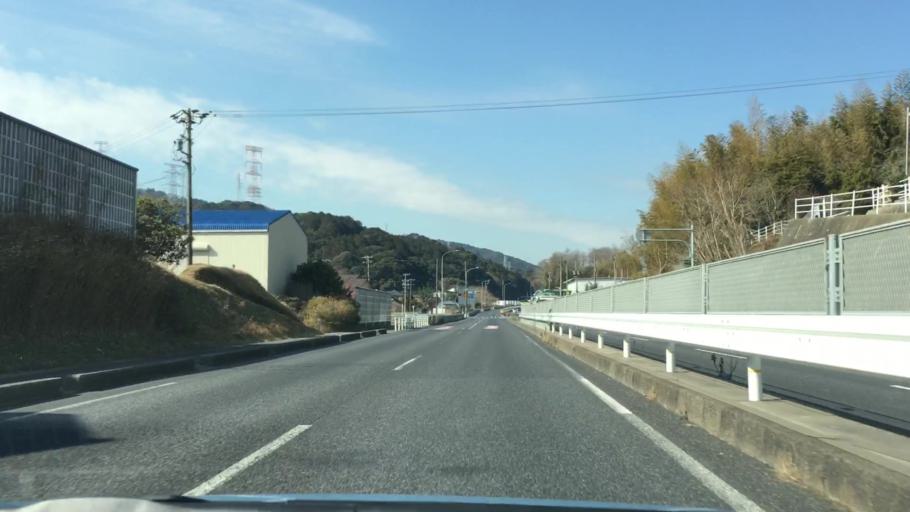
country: JP
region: Aichi
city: Gamagori
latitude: 34.8740
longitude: 137.2809
